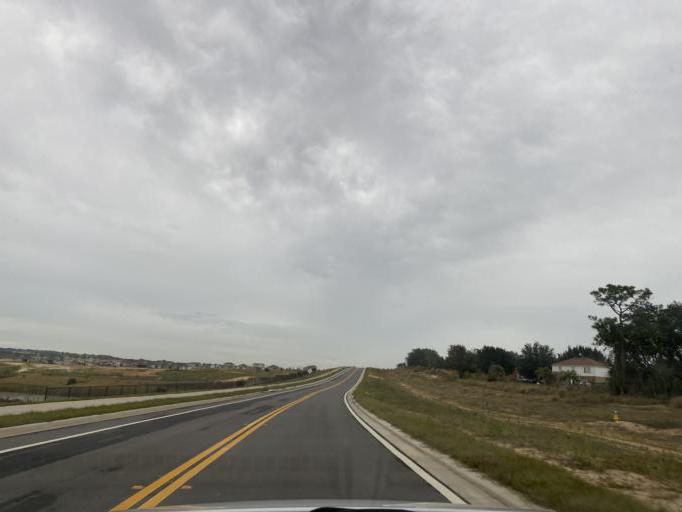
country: US
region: Florida
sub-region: Orange County
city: Oakland
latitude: 28.5313
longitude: -81.6908
